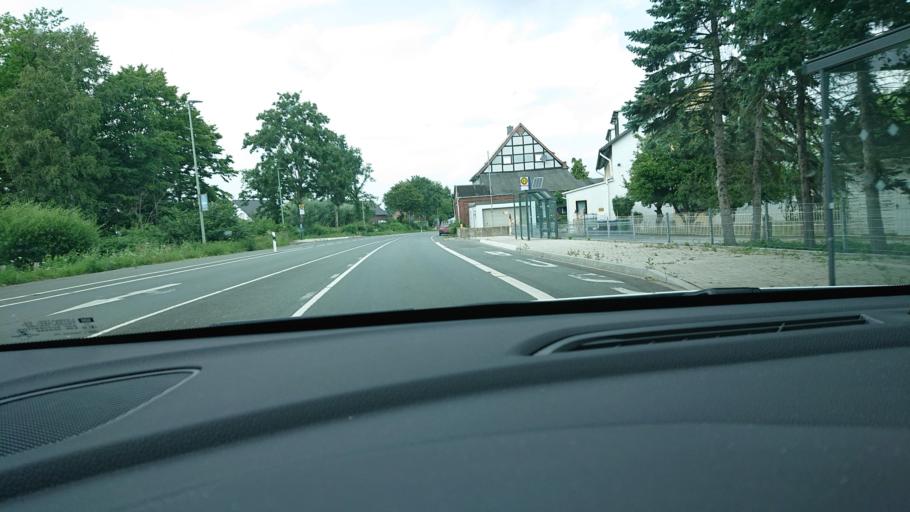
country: DE
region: North Rhine-Westphalia
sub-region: Regierungsbezirk Arnsberg
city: Bad Sassendorf
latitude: 51.5449
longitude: 8.1460
